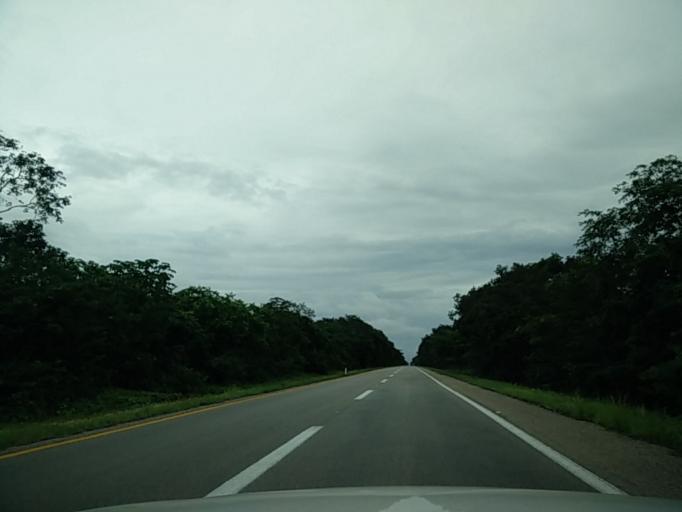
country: MX
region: Quintana Roo
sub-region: Lazaro Cardenas
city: Ignacio Zaragoza
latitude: 20.8885
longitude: -87.5422
